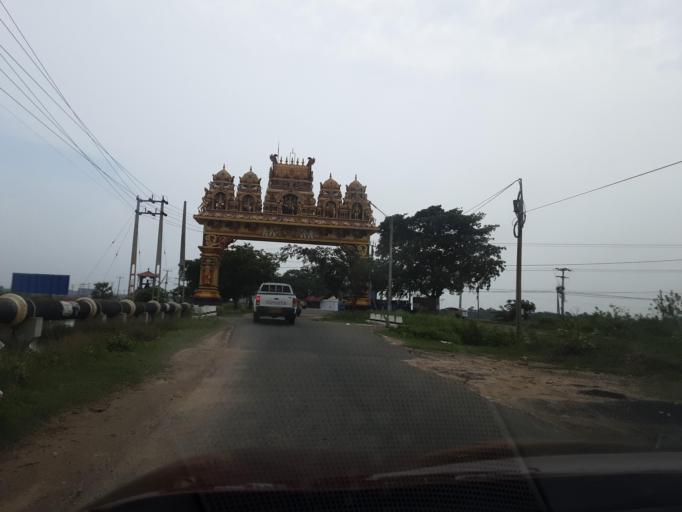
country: LK
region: Northern Province
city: Jaffna
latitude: 9.6632
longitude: 80.0615
